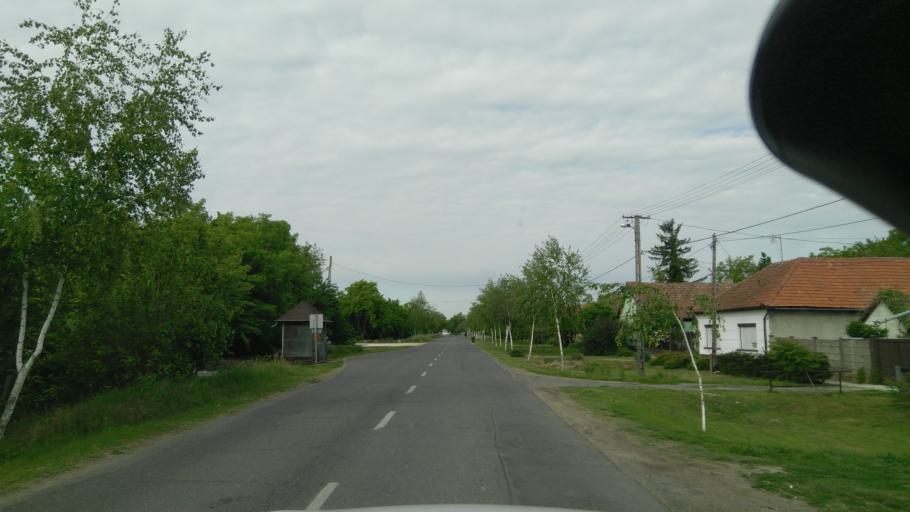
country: HU
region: Bekes
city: Ketegyhaza
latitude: 46.5508
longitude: 21.1864
